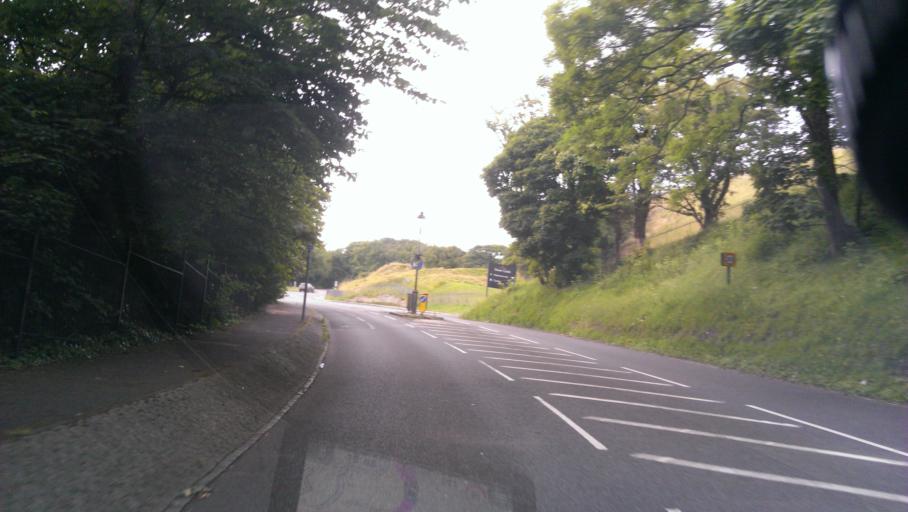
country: GB
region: England
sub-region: Kent
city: Dover
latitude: 51.1303
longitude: 1.3191
